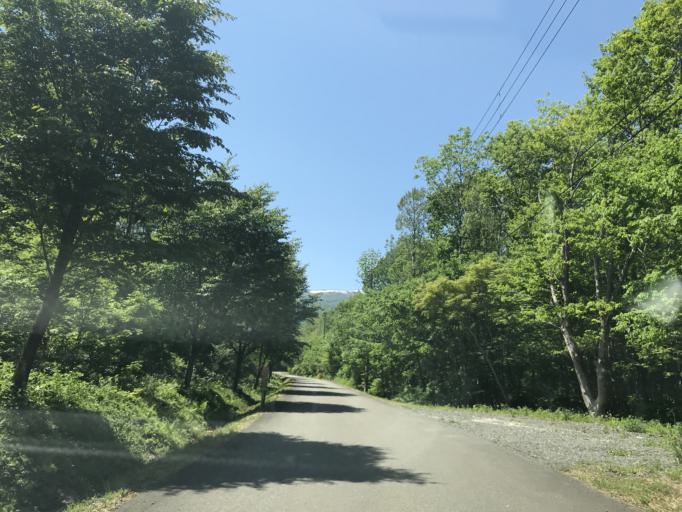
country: JP
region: Iwate
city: Shizukuishi
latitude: 39.5445
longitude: 140.8255
